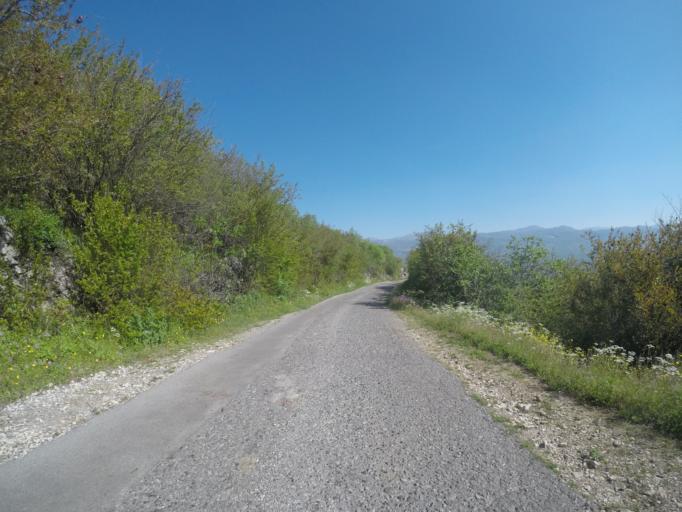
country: ME
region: Danilovgrad
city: Danilovgrad
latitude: 42.5148
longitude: 19.0979
